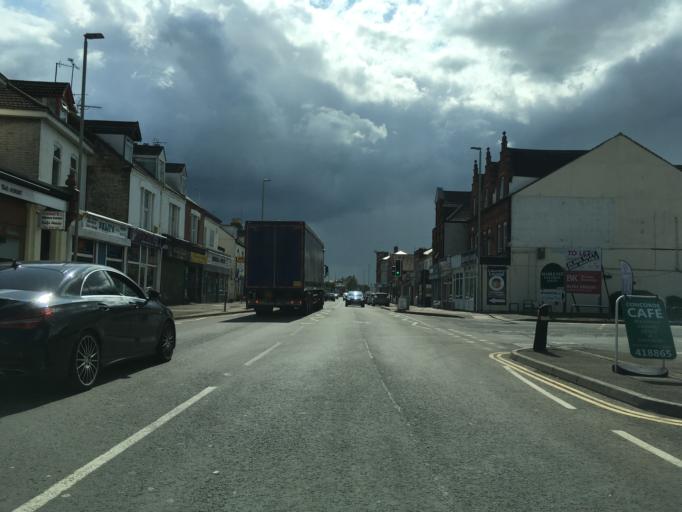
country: GB
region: England
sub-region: Gloucestershire
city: Gloucester
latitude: 51.8558
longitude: -2.2522
